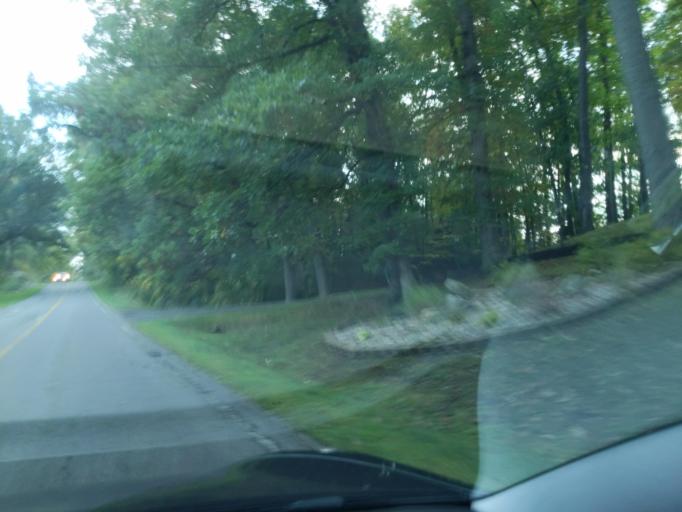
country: US
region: Michigan
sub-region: Jackson County
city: Jackson
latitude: 42.2899
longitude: -84.4831
